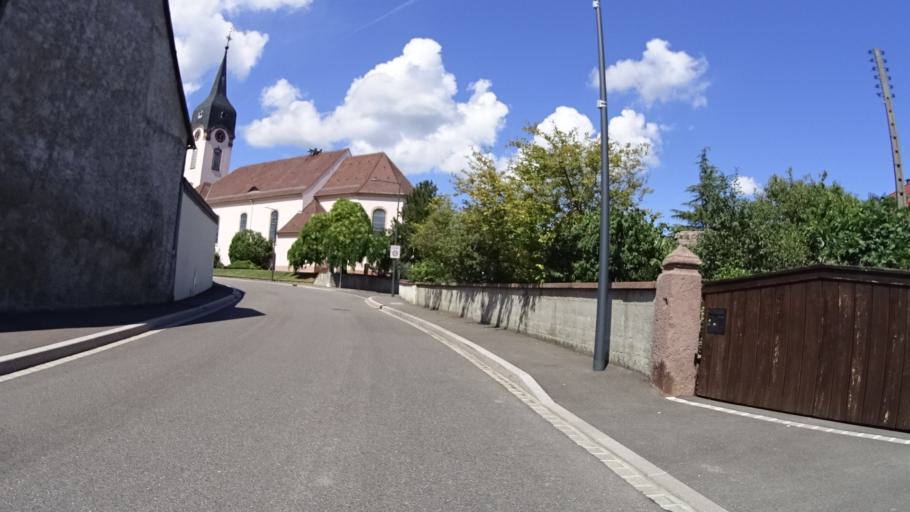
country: FR
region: Alsace
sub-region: Departement du Haut-Rhin
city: Bantzenheim
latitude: 47.8248
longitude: 7.5174
